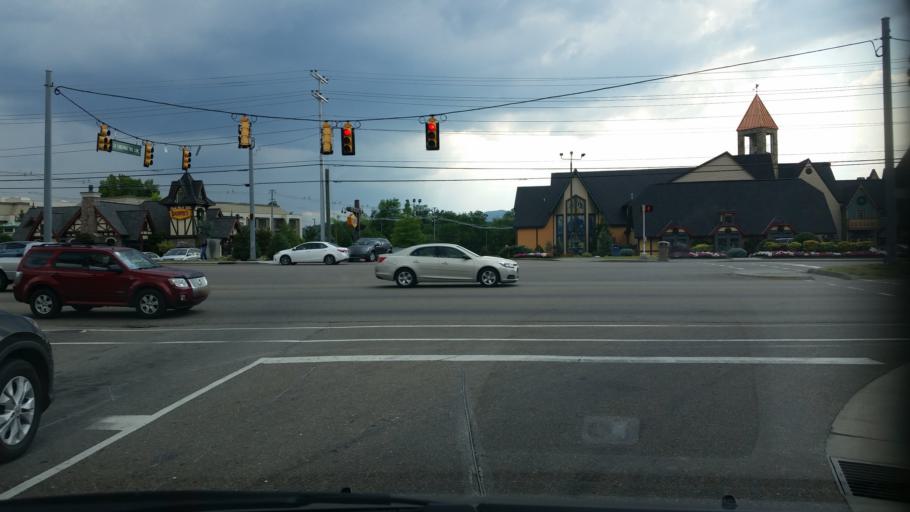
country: US
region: Tennessee
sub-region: Sevier County
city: Pigeon Forge
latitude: 35.8093
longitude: -83.5776
